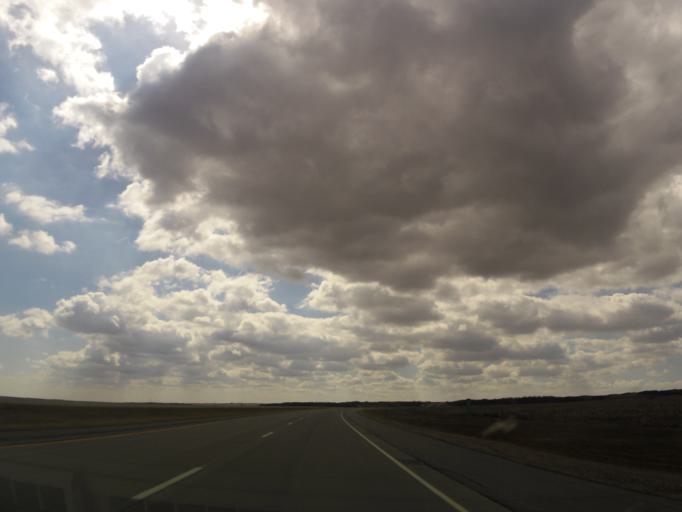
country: US
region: South Dakota
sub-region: Roberts County
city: Sisseton
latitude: 45.4428
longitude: -96.9903
